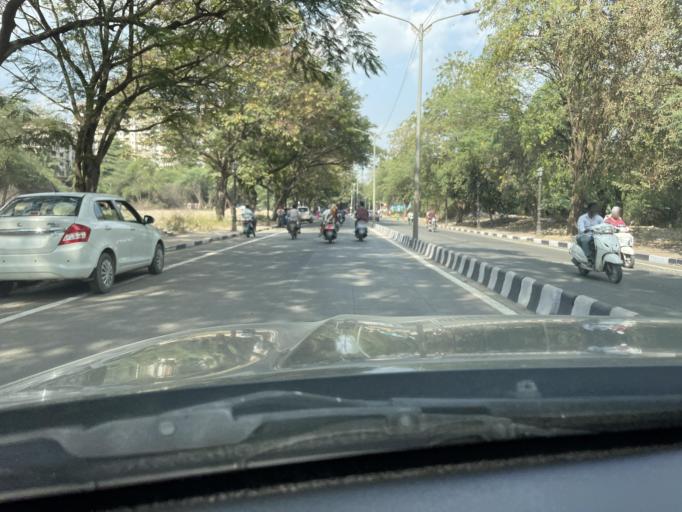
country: IN
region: Maharashtra
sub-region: Pune Division
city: Pune
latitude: 18.4880
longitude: 73.9000
